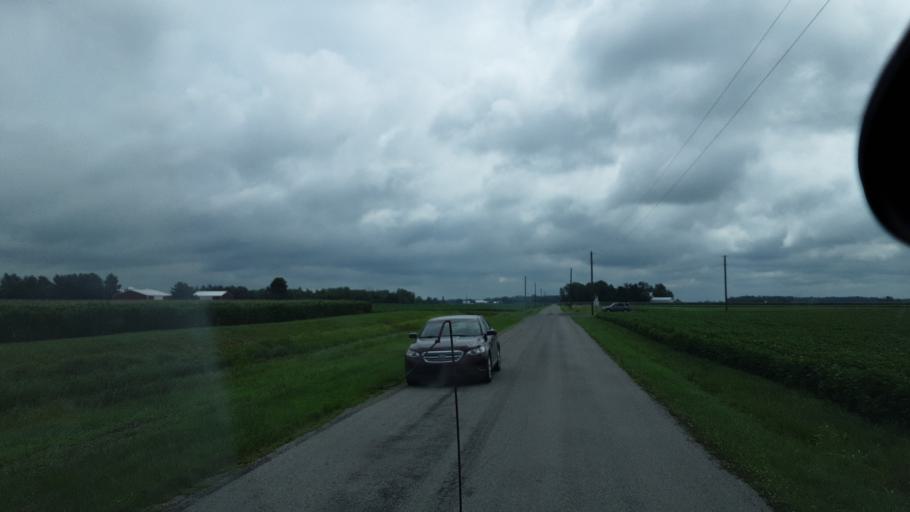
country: US
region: Indiana
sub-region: Wells County
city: Ossian
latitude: 40.8594
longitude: -85.1029
